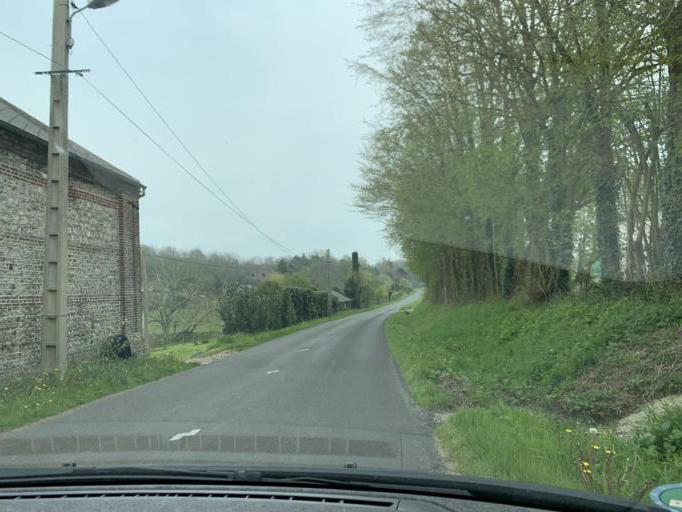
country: FR
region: Haute-Normandie
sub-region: Departement de la Seine-Maritime
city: Saint-Valery-en-Caux
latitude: 49.8571
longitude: 0.7229
